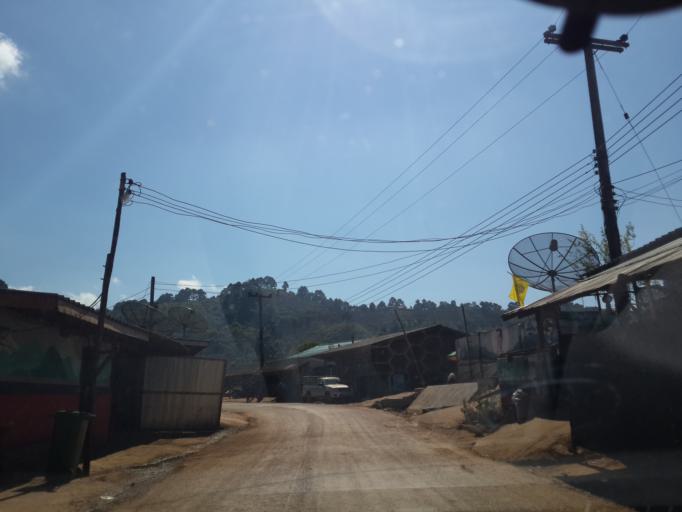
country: TH
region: Chiang Mai
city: Fang
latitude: 19.9371
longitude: 99.0411
